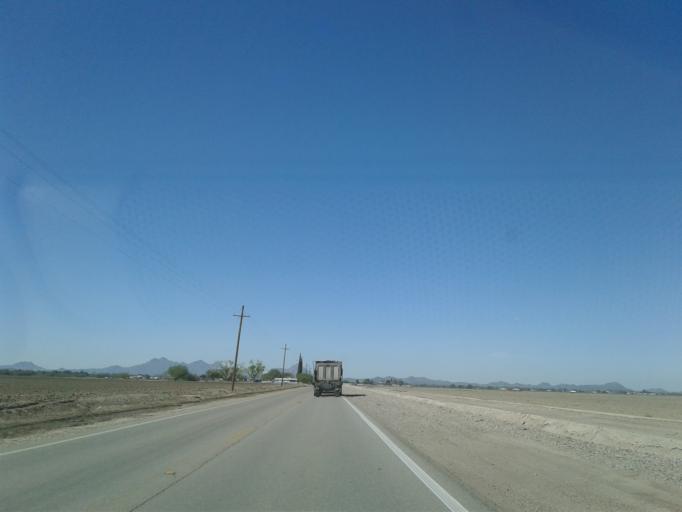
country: US
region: Arizona
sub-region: Pima County
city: Marana
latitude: 32.4605
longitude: -111.2562
